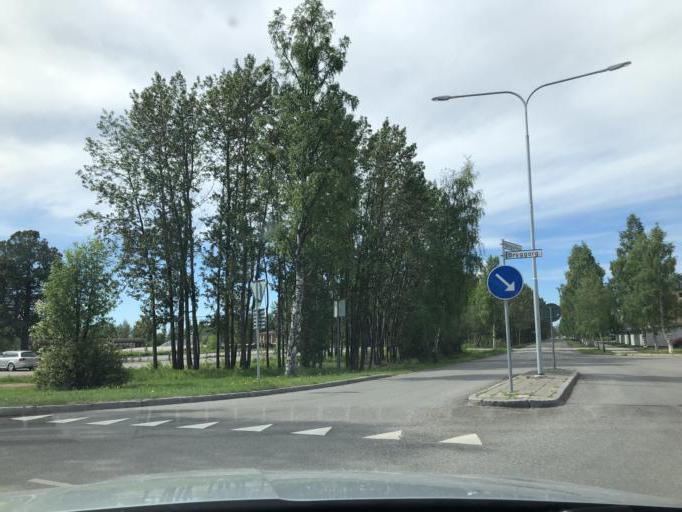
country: SE
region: Norrbotten
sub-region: Pitea Kommun
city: Pitea
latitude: 65.3193
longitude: 21.4730
